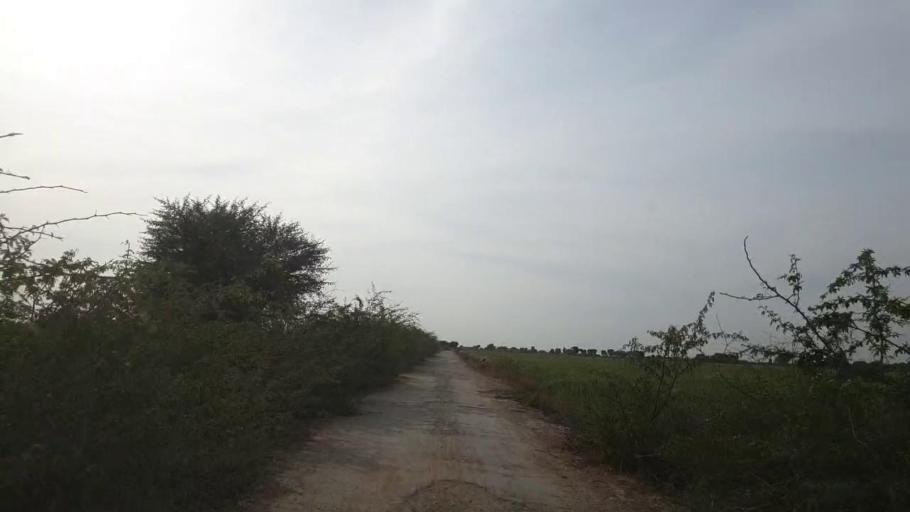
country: PK
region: Sindh
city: Nabisar
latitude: 25.0002
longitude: 69.5394
